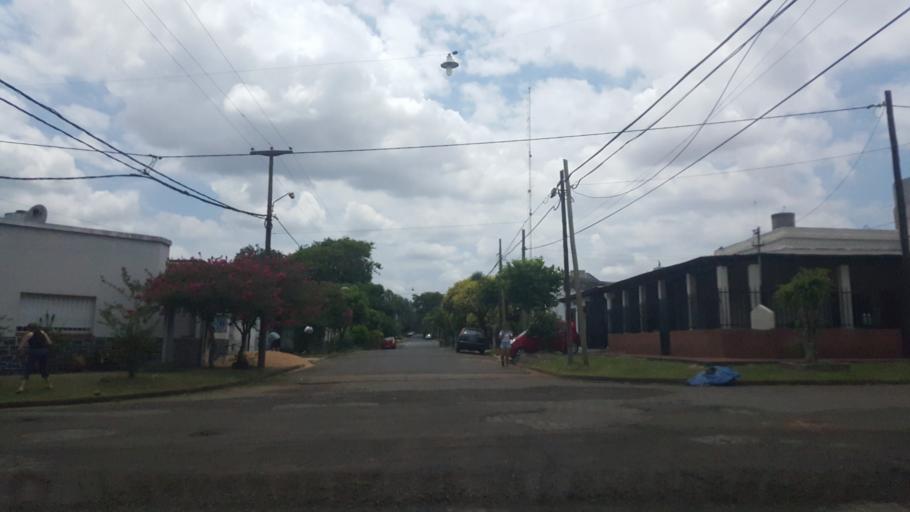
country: AR
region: Misiones
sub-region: Departamento de Capital
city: Posadas
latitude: -27.3836
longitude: -55.8980
